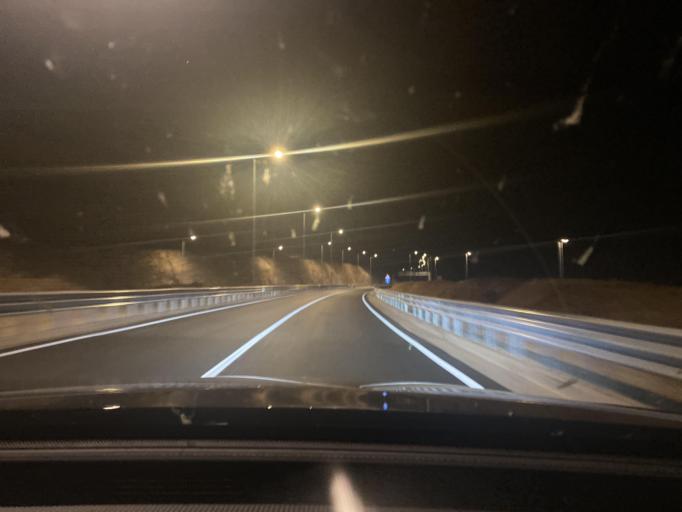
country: BA
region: Federation of Bosnia and Herzegovina
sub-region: Hercegovacko-Bosanski Kanton
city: Neum
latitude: 42.9072
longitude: 17.5380
